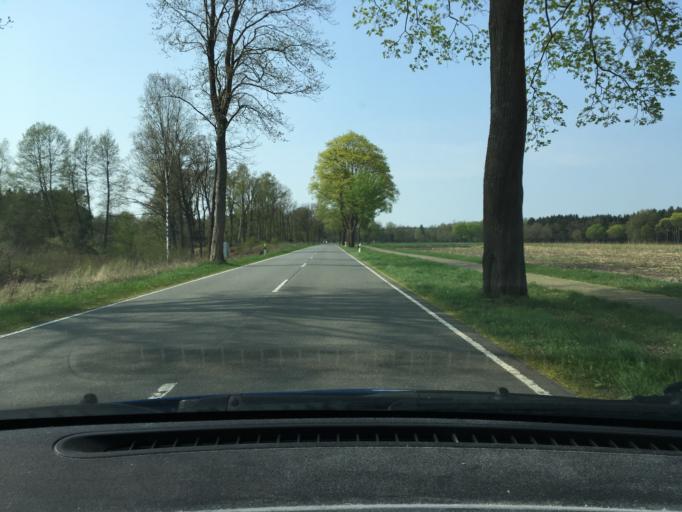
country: DE
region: Lower Saxony
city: Fassberg
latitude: 52.8857
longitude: 10.1804
